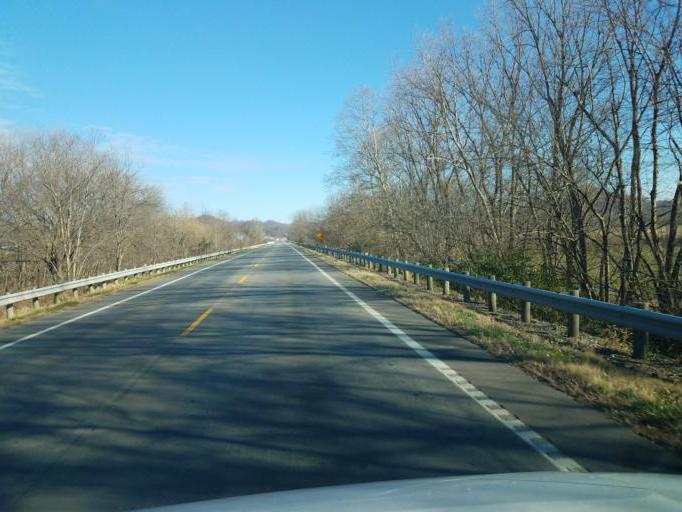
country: US
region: Ohio
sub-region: Scioto County
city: Lucasville
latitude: 38.8823
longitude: -83.0125
